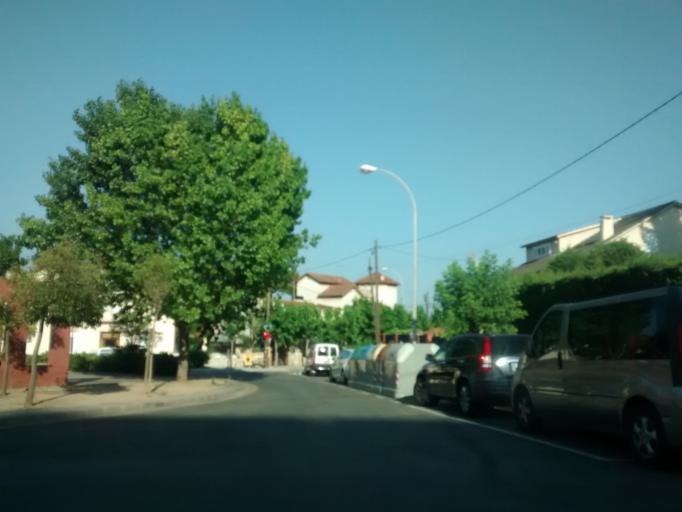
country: ES
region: Catalonia
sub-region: Provincia de Barcelona
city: Sant Vicenc dels Horts
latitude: 41.3878
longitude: 2.0110
